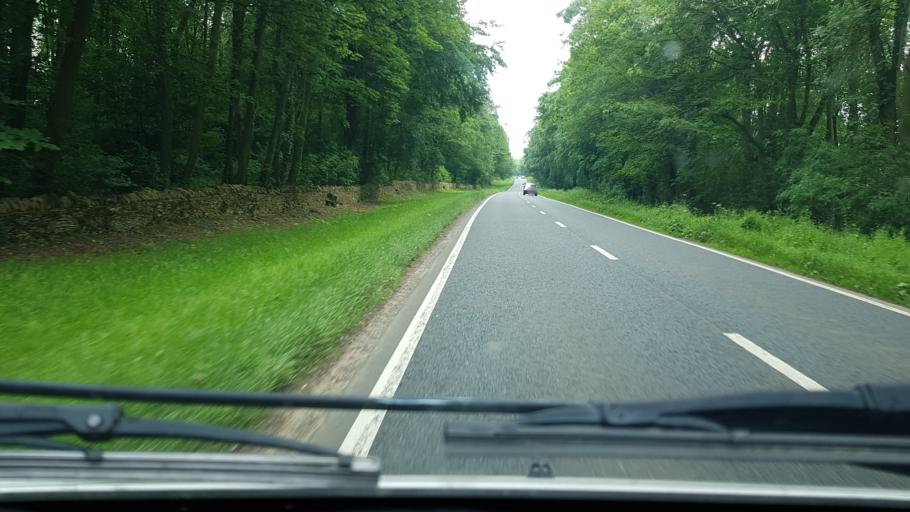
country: GB
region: England
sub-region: Gloucestershire
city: Chipping Campden
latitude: 52.0112
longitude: -1.7952
